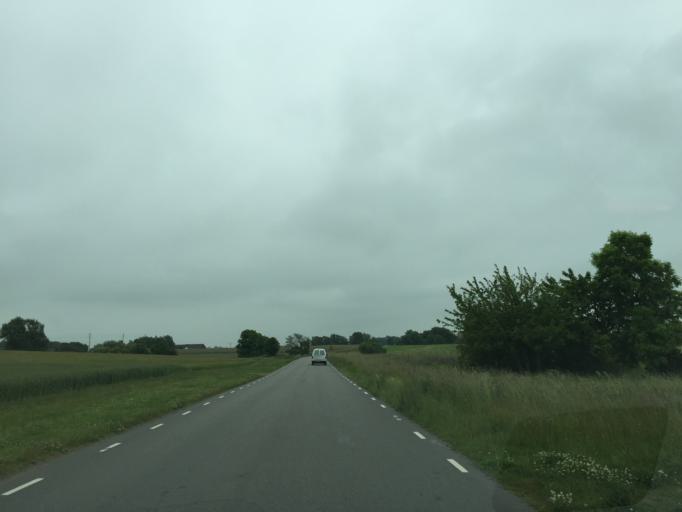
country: SE
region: Skane
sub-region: Ystads Kommun
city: Kopingebro
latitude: 55.4484
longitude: 14.0262
